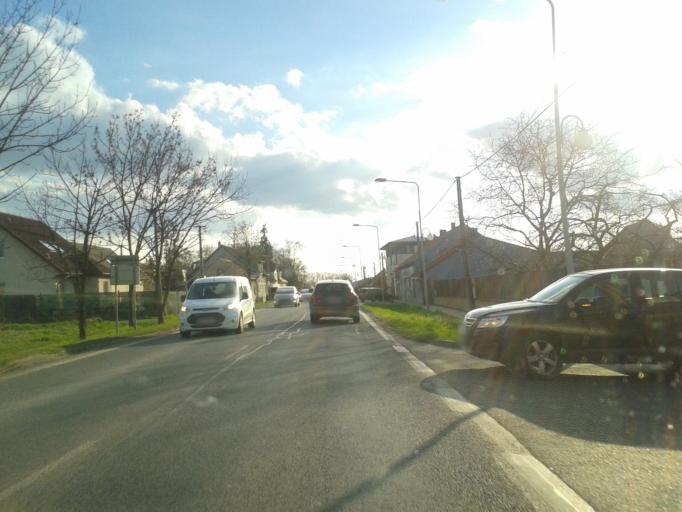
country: CZ
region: Central Bohemia
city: Rudna
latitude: 50.0461
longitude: 14.2615
